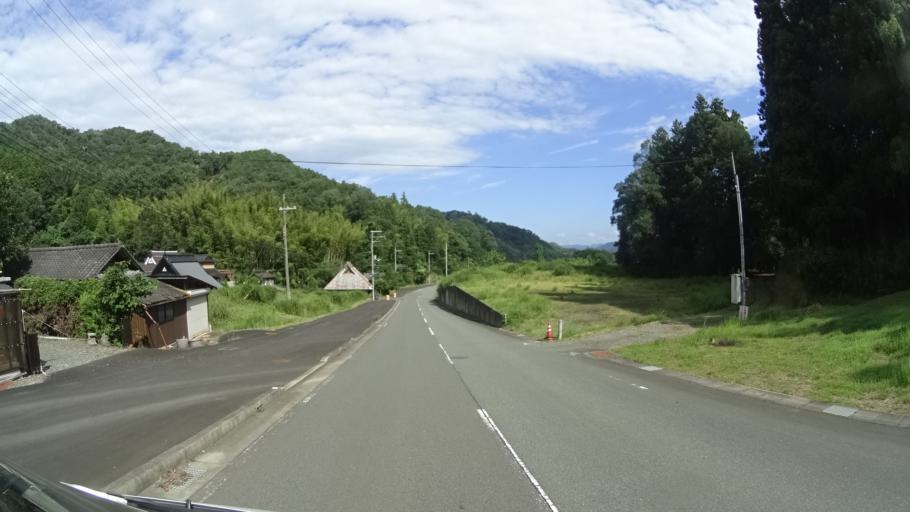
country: JP
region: Kyoto
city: Fukuchiyama
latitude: 35.3421
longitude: 135.1626
